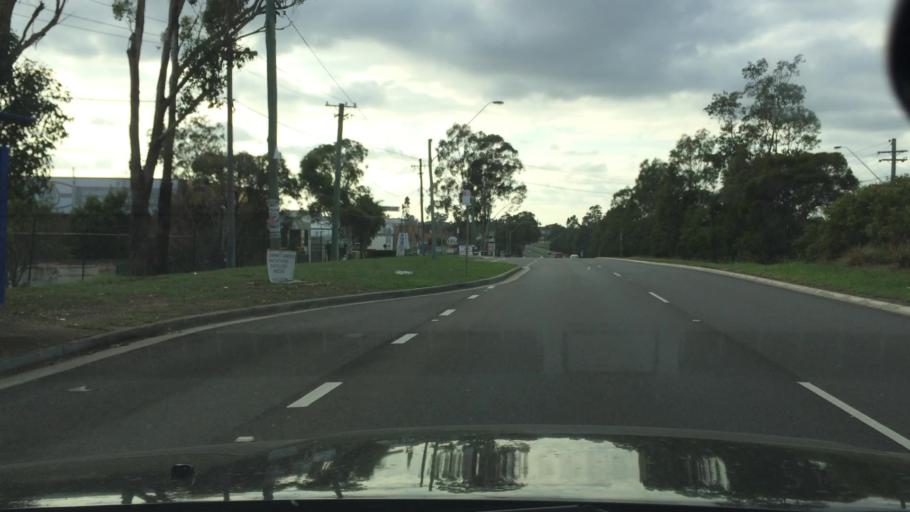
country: AU
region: New South Wales
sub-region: Fairfield
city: Horsley Park
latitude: -33.8524
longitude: 150.8812
